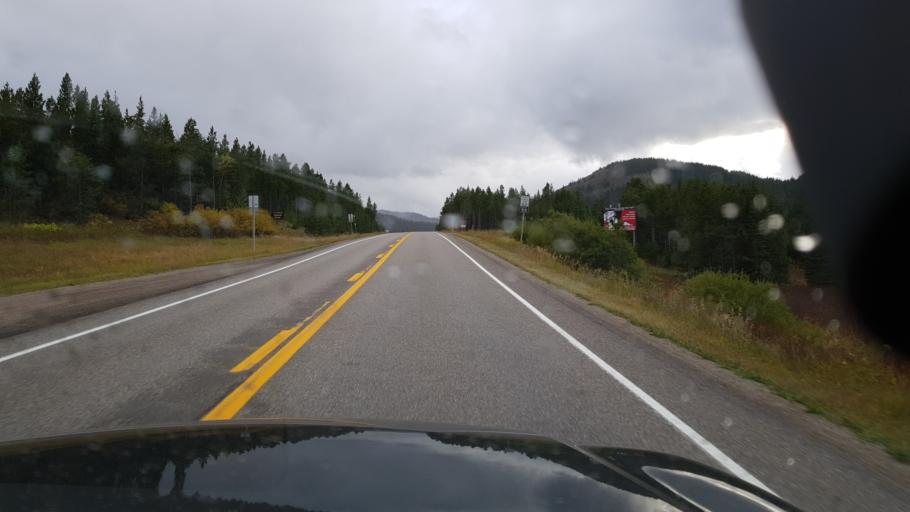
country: US
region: Montana
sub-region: Glacier County
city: South Browning
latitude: 48.3144
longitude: -113.3570
